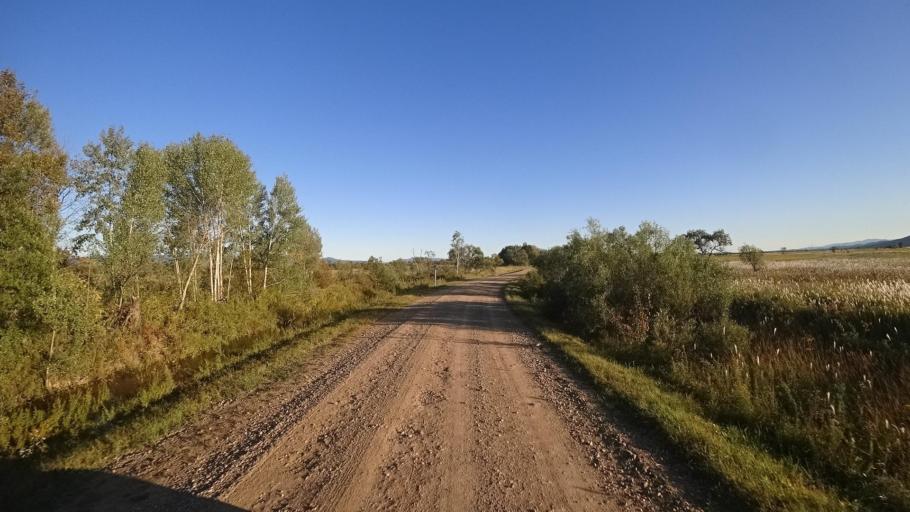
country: RU
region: Primorskiy
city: Kirovskiy
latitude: 44.8128
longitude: 133.6160
